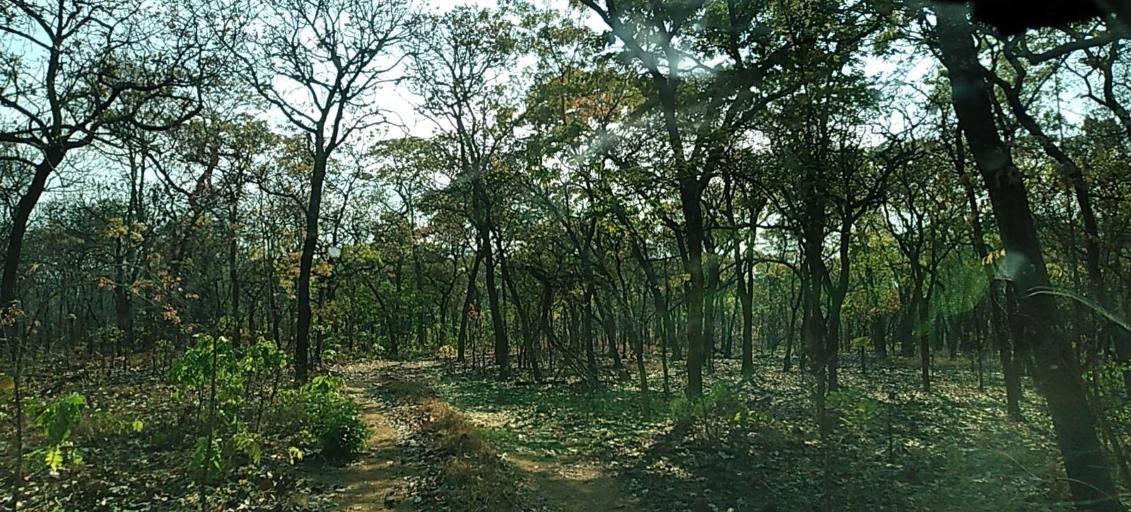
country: ZM
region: North-Western
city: Kalengwa
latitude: -13.2294
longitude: 25.0780
